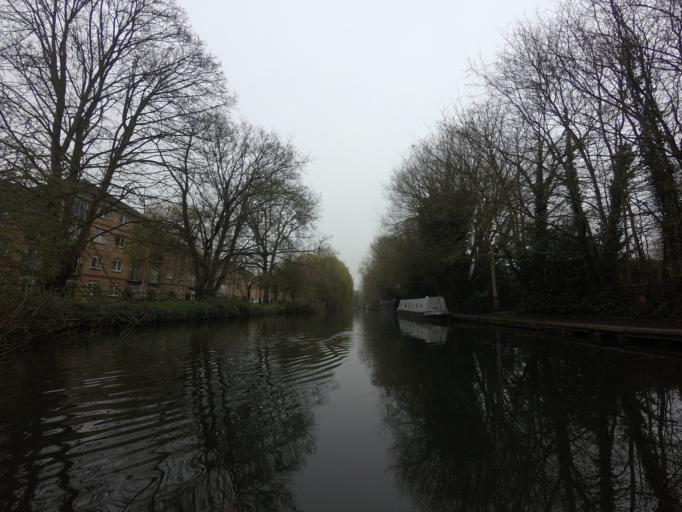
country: GB
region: England
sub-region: Hertfordshire
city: Kings Langley
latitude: 51.7311
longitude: -0.4570
